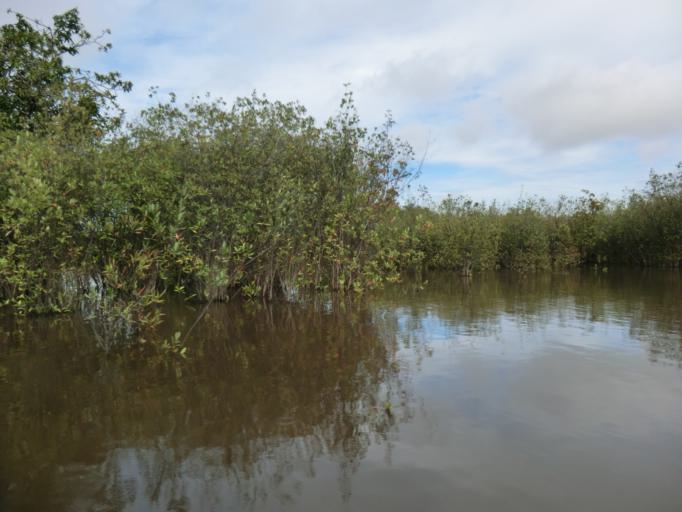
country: MY
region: Sarawak
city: Simanggang
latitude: 0.8879
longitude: 111.9731
